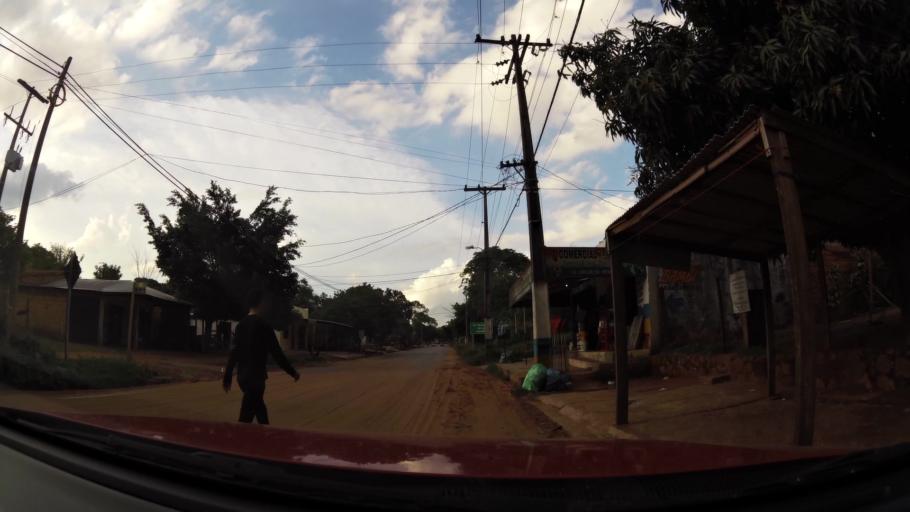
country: PY
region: Central
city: Nemby
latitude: -25.3694
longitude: -57.5418
